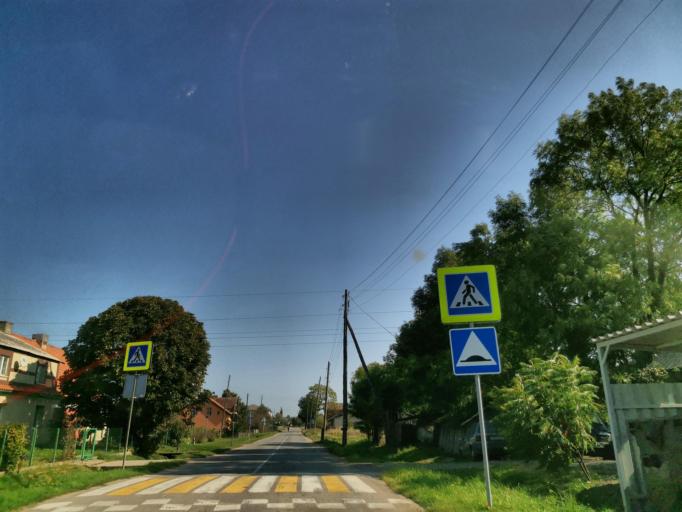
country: RU
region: Kaliningrad
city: Neman
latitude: 54.8214
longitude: 22.0764
